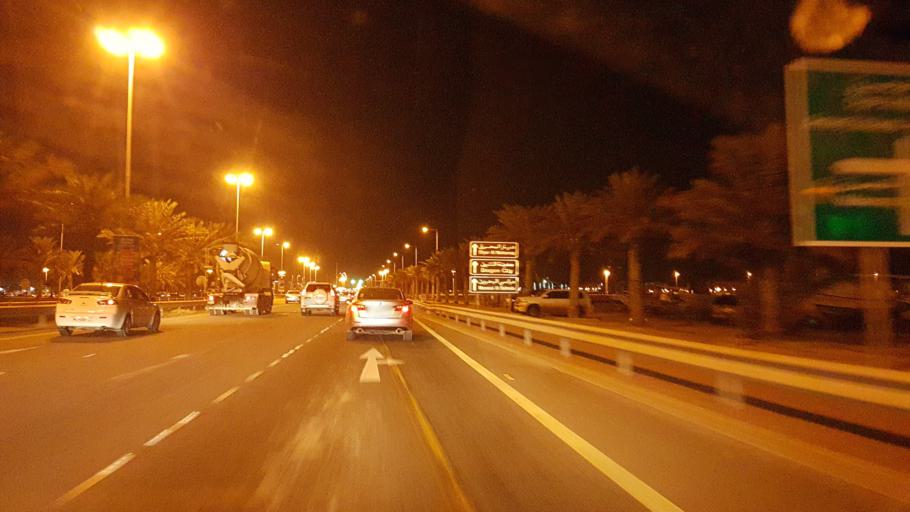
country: BH
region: Muharraq
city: Al Hadd
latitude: 26.2511
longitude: 50.6594
